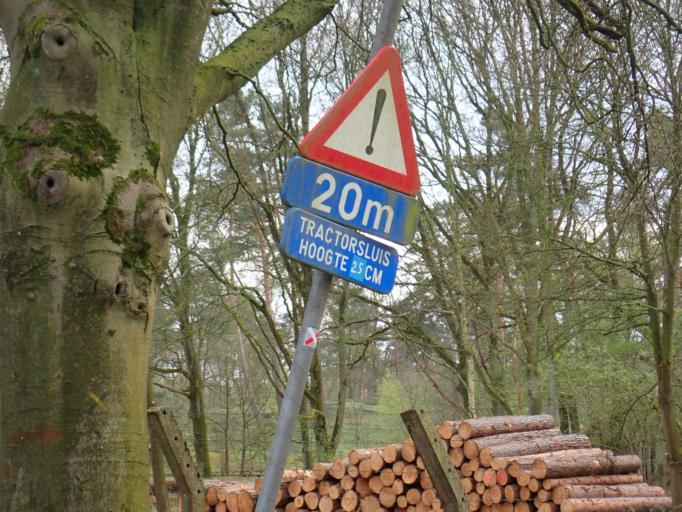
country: BE
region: Flanders
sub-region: Provincie Antwerpen
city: Vorselaar
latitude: 51.1842
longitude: 4.7837
